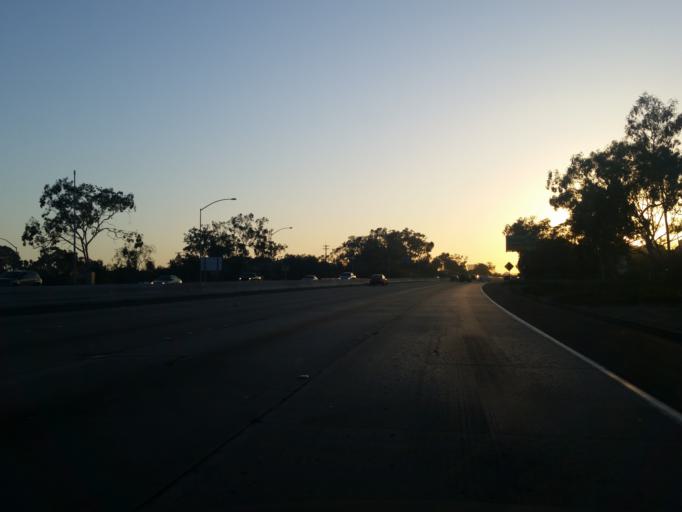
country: US
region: California
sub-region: San Diego County
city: San Diego
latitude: 32.7136
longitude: -117.1317
